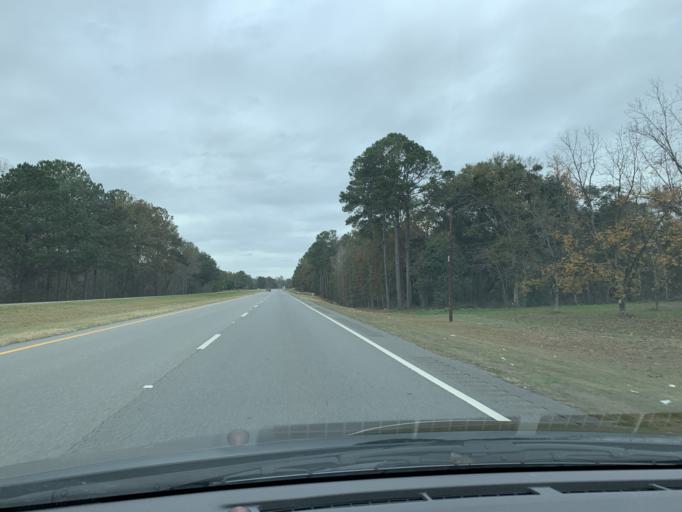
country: US
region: Georgia
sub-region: Thomas County
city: Thomasville
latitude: 30.9407
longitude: -84.0141
